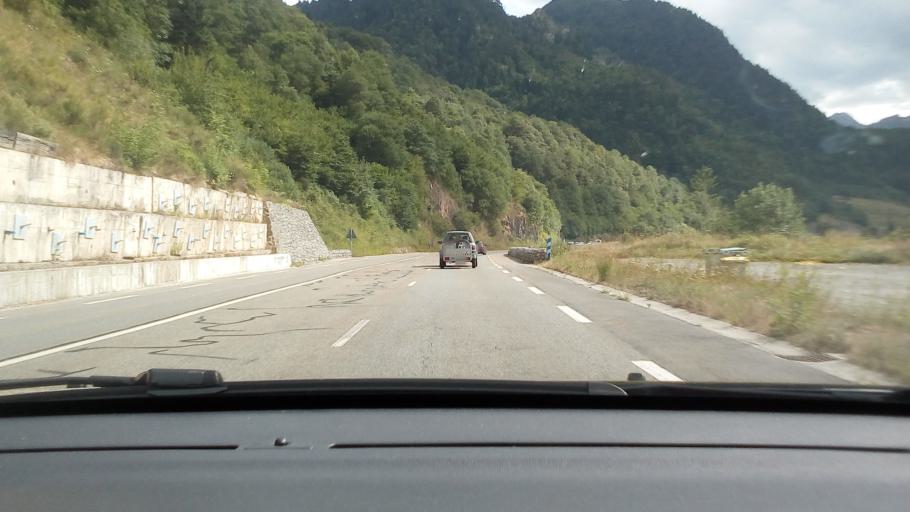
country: ES
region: Aragon
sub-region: Provincia de Huesca
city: Canfranc
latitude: 42.8531
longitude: -0.5489
